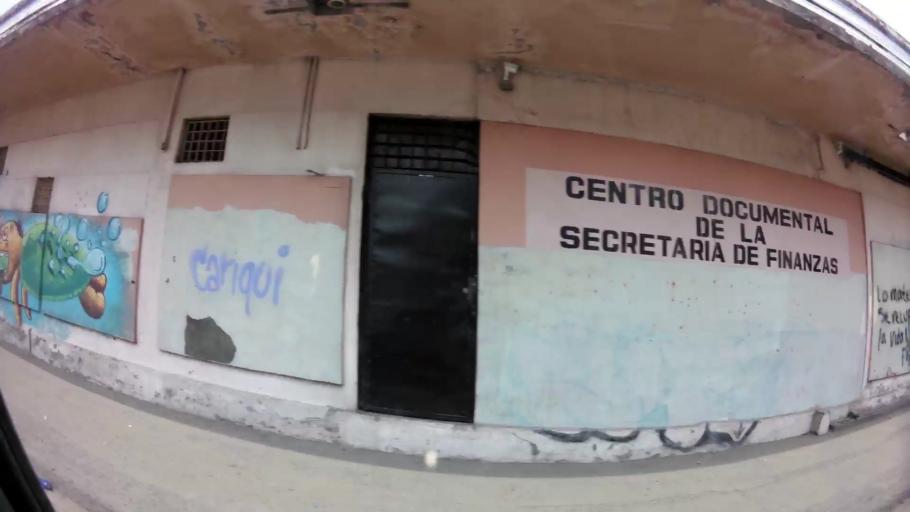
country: HN
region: Francisco Morazan
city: Tegucigalpa
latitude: 14.0890
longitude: -87.2078
